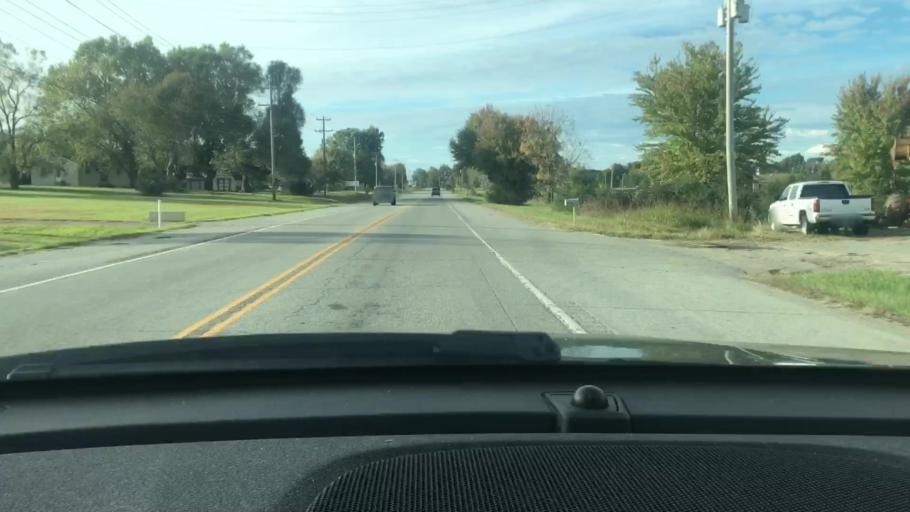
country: US
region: Tennessee
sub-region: Dickson County
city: White Bluff
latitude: 36.1348
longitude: -87.2366
